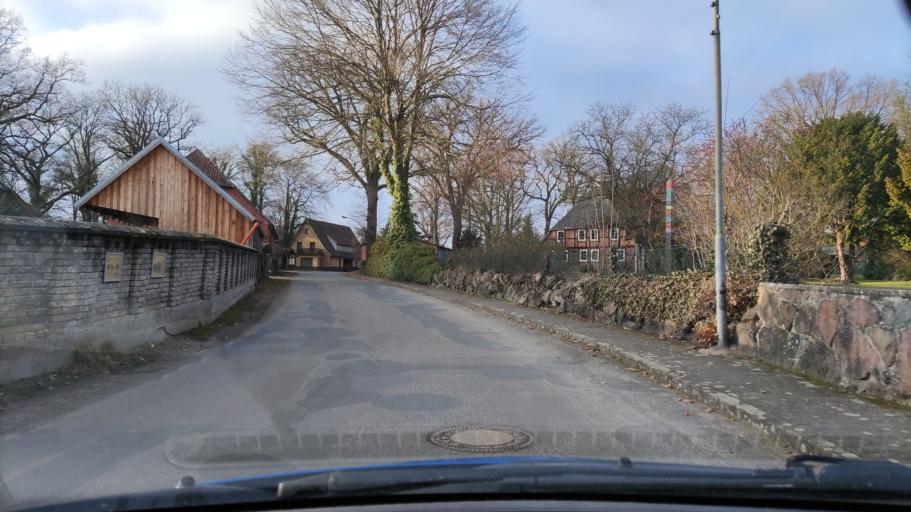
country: DE
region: Lower Saxony
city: Suderburg
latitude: 52.9295
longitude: 10.4417
